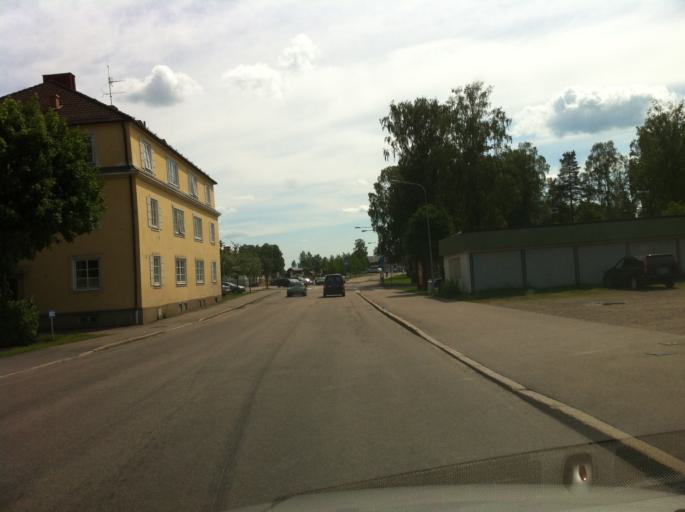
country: SE
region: Vaermland
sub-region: Sunne Kommun
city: Sunne
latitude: 59.8373
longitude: 13.1481
